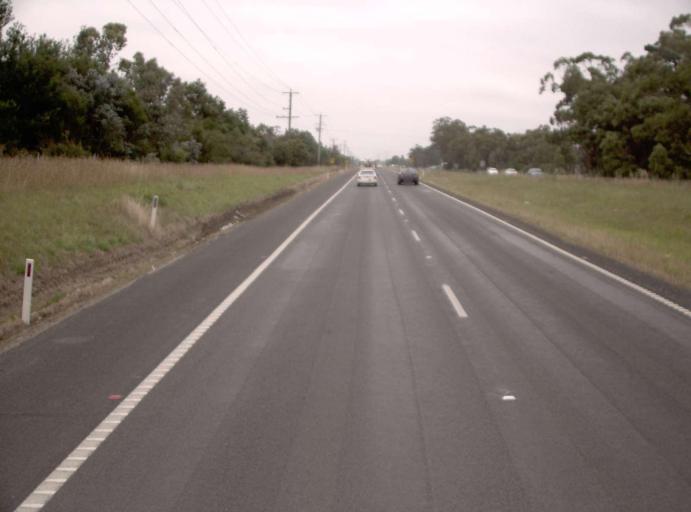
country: AU
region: Victoria
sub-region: Latrobe
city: Traralgon
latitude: -38.2132
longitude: 146.4833
